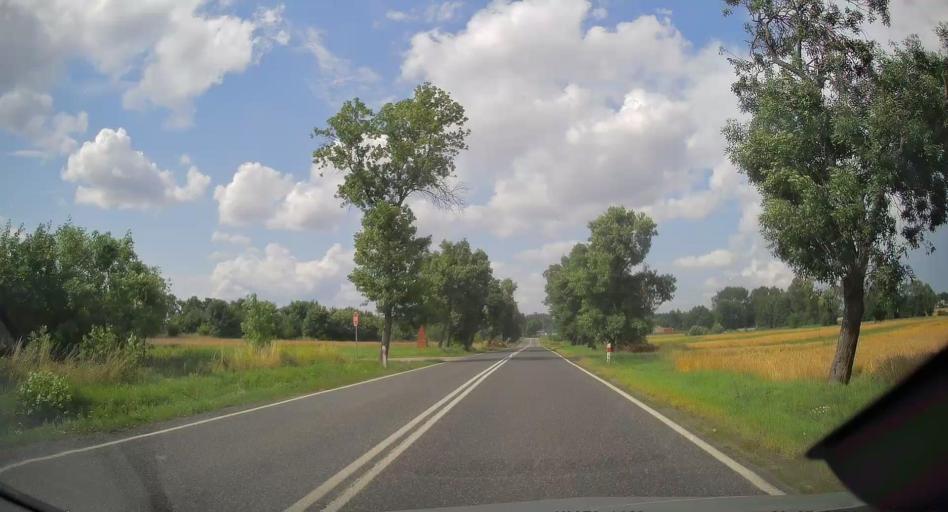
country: PL
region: Lodz Voivodeship
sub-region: Powiat brzezinski
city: Jezow
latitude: 51.8042
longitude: 20.0148
